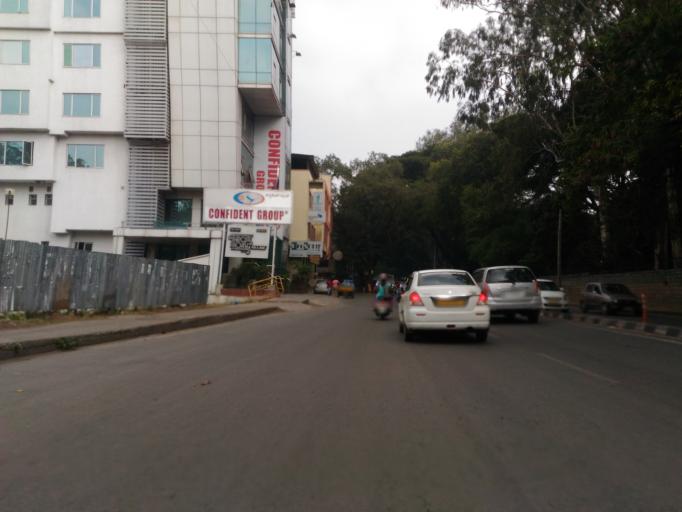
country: IN
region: Karnataka
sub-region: Bangalore Urban
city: Bangalore
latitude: 12.9557
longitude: 77.6056
